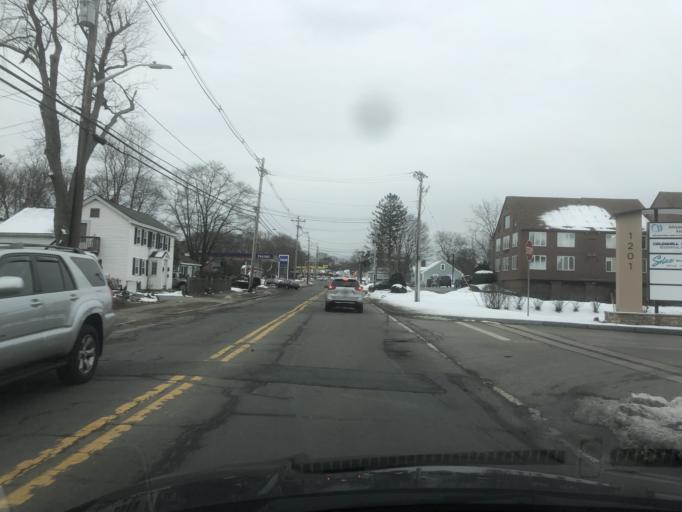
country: US
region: Massachusetts
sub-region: Middlesex County
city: Tewksbury
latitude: 42.6076
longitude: -71.2276
